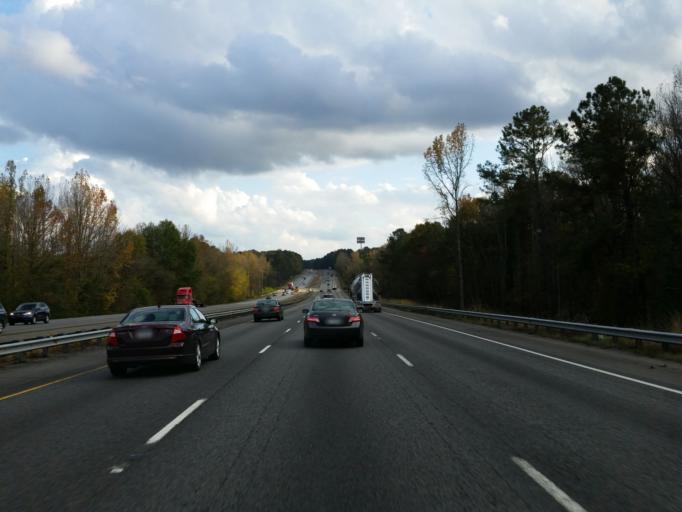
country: US
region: Georgia
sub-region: Henry County
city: Locust Grove
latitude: 33.2408
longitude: -84.0831
